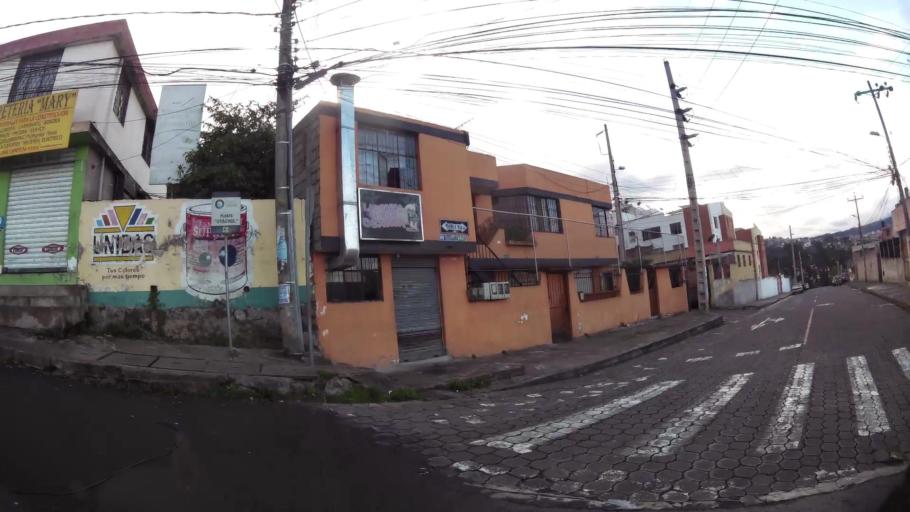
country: EC
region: Pichincha
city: Quito
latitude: -0.1128
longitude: -78.5090
